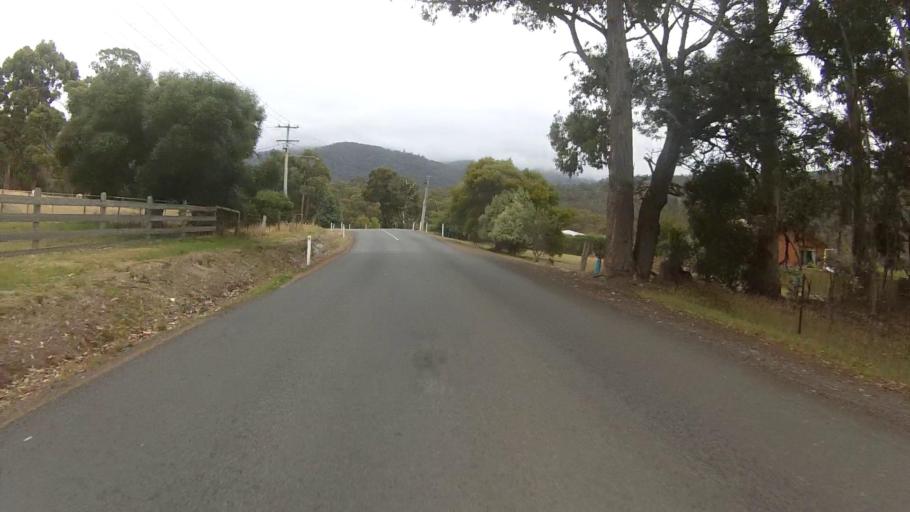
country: AU
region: Tasmania
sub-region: Kingborough
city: Kingston
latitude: -42.9637
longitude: 147.2819
